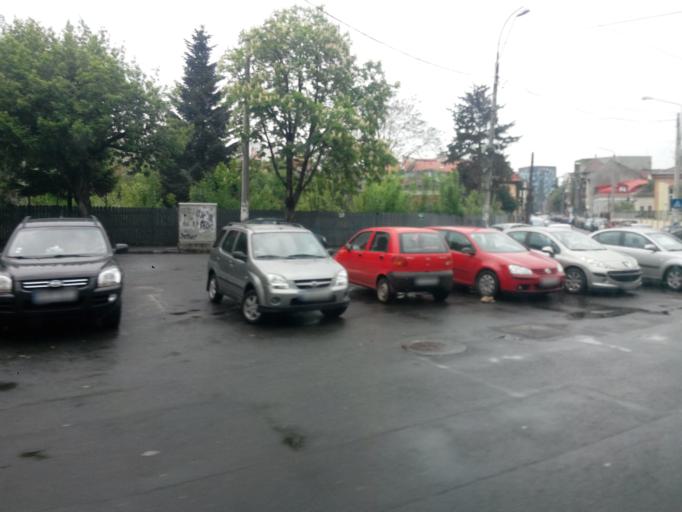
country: RO
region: Bucuresti
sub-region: Municipiul Bucuresti
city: Bucharest
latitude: 44.4390
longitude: 26.1181
